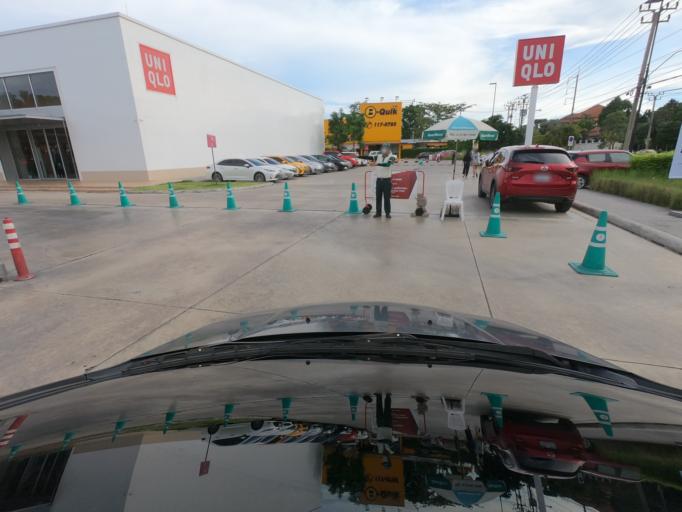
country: TH
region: Bangkok
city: Bang Na
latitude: 13.6575
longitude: 100.6233
